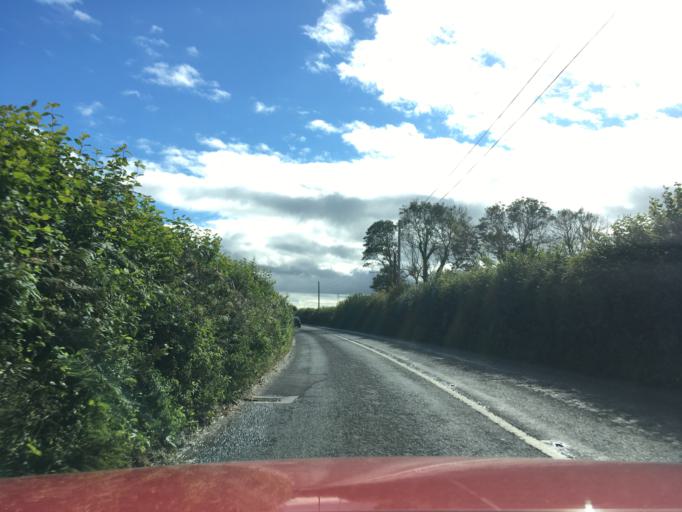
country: GB
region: England
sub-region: Devon
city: Kingsbridge
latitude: 50.3406
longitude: -3.7391
